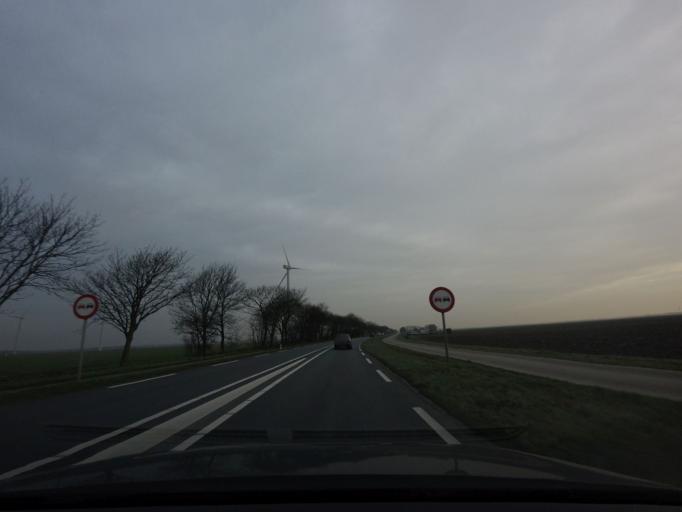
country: NL
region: North Holland
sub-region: Gemeente Opmeer
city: Opmeer
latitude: 52.7717
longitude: 4.9541
